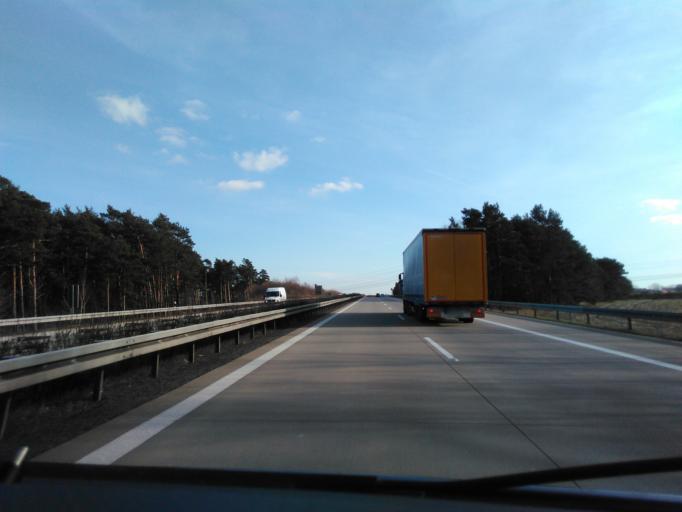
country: DE
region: Brandenburg
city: Luebben
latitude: 51.9068
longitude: 13.8019
